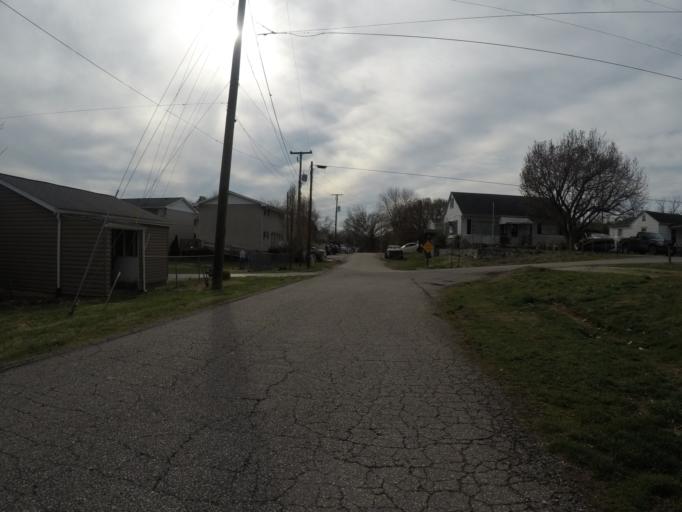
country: US
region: West Virginia
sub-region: Cabell County
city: Huntington
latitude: 38.4213
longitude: -82.4798
